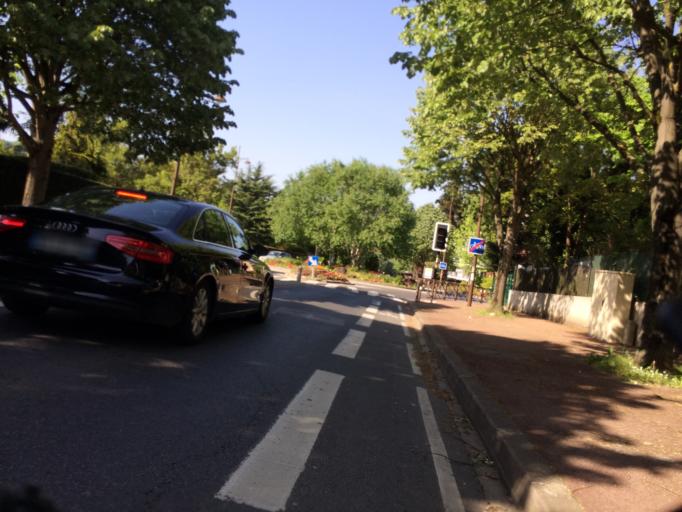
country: FR
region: Ile-de-France
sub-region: Departement des Hauts-de-Seine
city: Chatenay-Malabry
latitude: 48.7697
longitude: 2.2740
